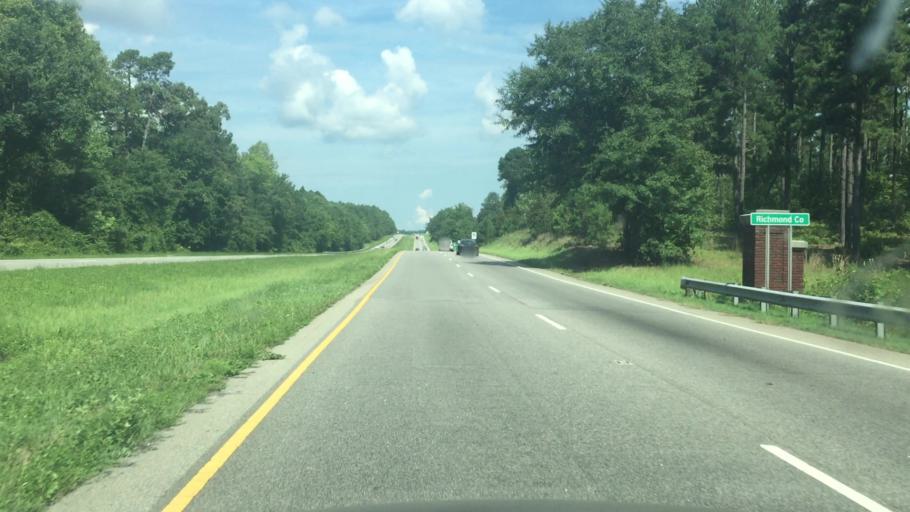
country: US
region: North Carolina
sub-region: Richmond County
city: Hamlet
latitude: 34.8553
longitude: -79.6242
